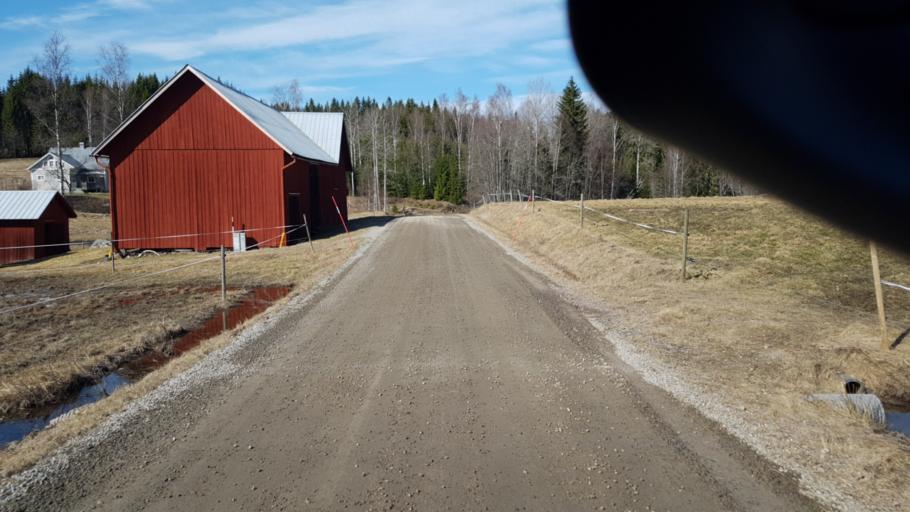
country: SE
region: Vaermland
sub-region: Arvika Kommun
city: Arvika
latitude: 59.6763
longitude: 12.7681
